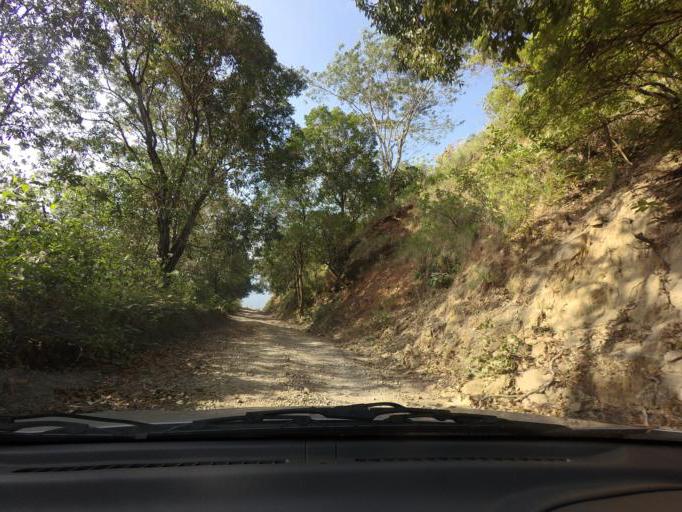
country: IN
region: Karnataka
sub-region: Kodagu
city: Somvarpet
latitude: 12.7112
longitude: 75.6782
